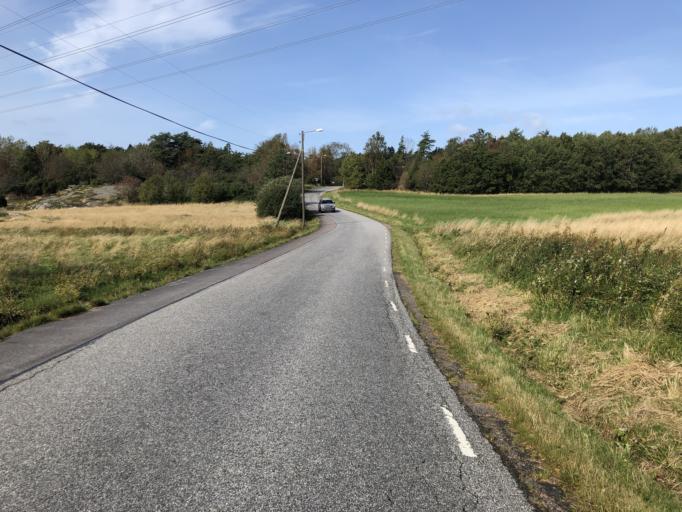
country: SE
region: Vaestra Goetaland
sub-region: Goteborg
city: Torslanda
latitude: 57.7351
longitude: 11.8408
